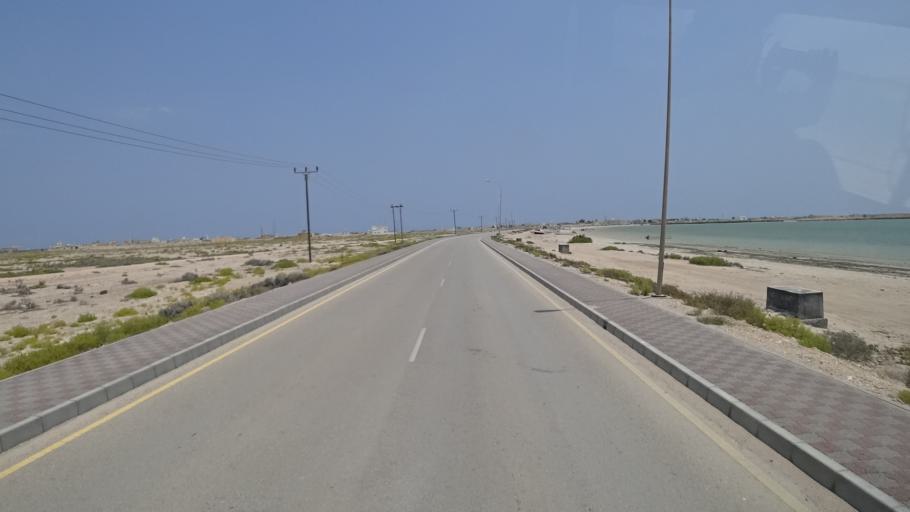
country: OM
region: Ash Sharqiyah
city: Sur
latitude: 22.5291
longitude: 59.7772
